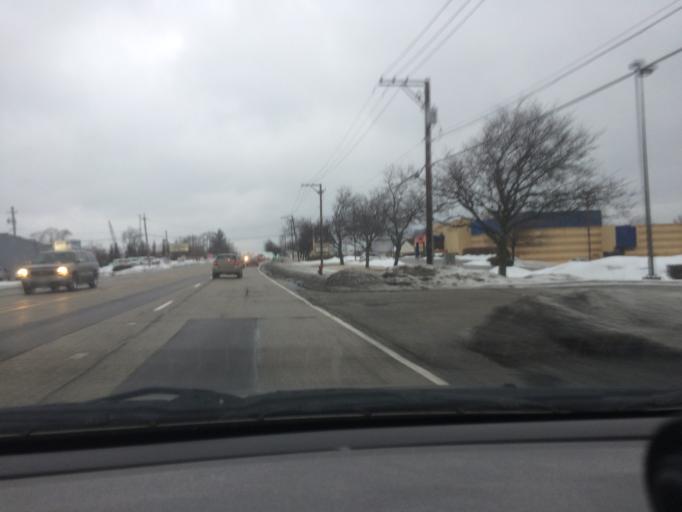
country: US
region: Illinois
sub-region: DuPage County
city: Bloomingdale
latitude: 41.9672
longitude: -88.1088
